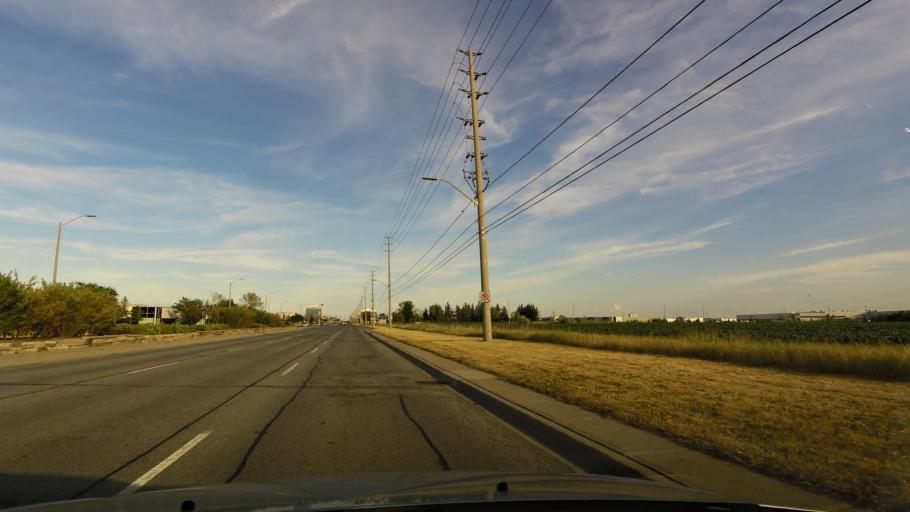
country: CA
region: Ontario
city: Brampton
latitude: 43.6426
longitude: -79.7017
